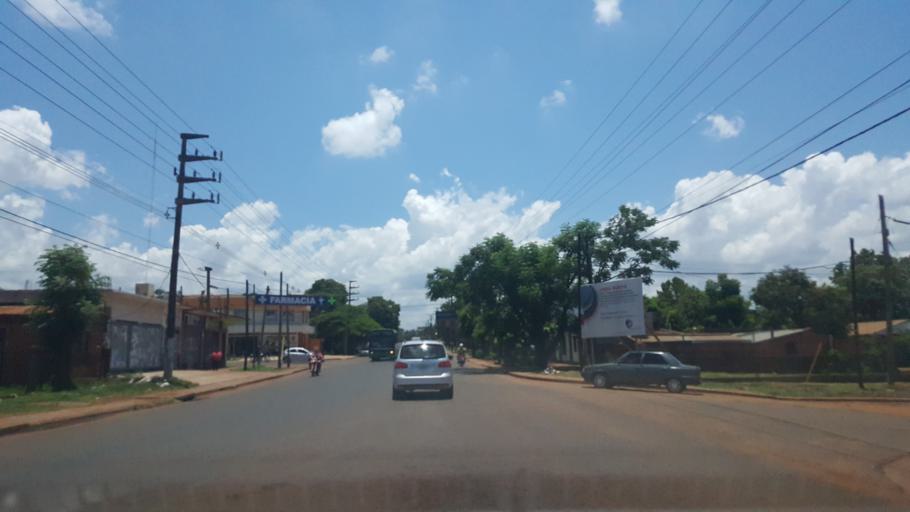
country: AR
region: Misiones
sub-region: Departamento de Capital
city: Posadas
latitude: -27.4077
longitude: -55.9115
